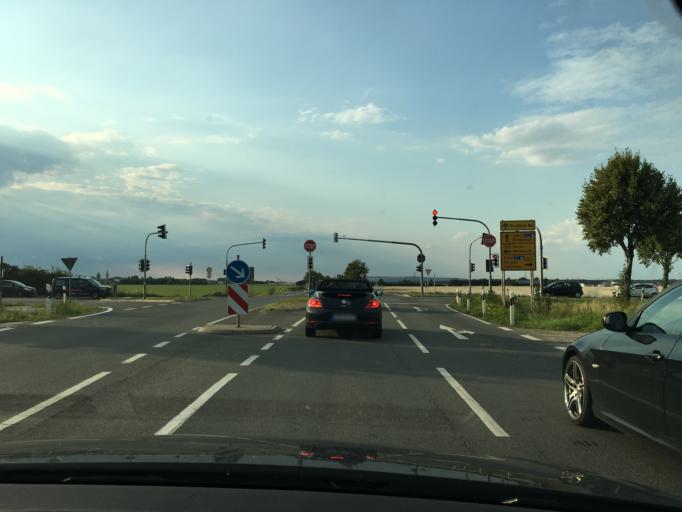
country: DE
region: North Rhine-Westphalia
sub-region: Regierungsbezirk Koln
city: Merzenich
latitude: 50.8226
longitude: 6.5432
